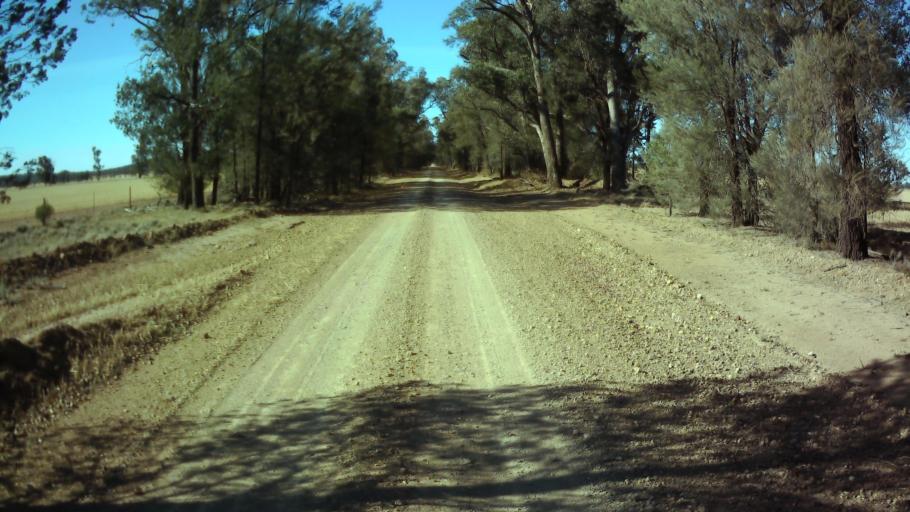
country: AU
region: New South Wales
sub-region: Weddin
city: Grenfell
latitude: -33.8222
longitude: 147.8751
